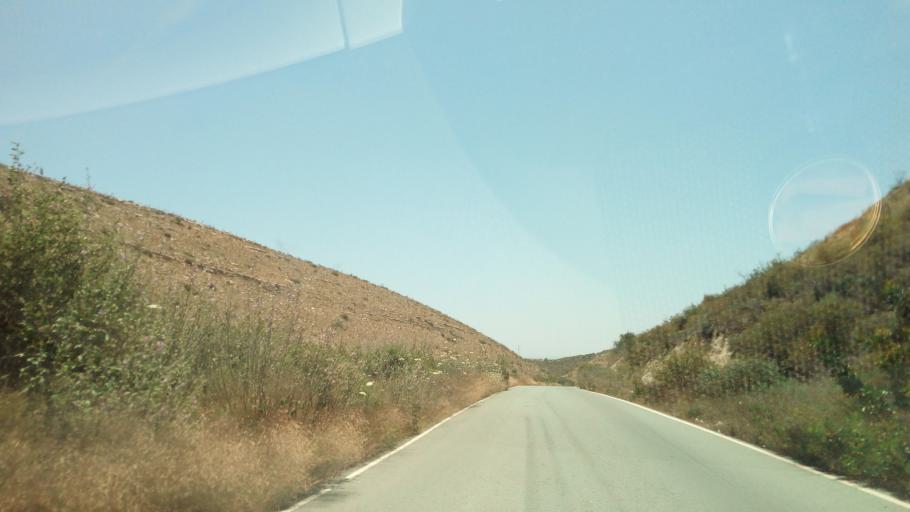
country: CY
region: Limassol
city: Ypsonas
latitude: 34.7320
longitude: 32.9485
